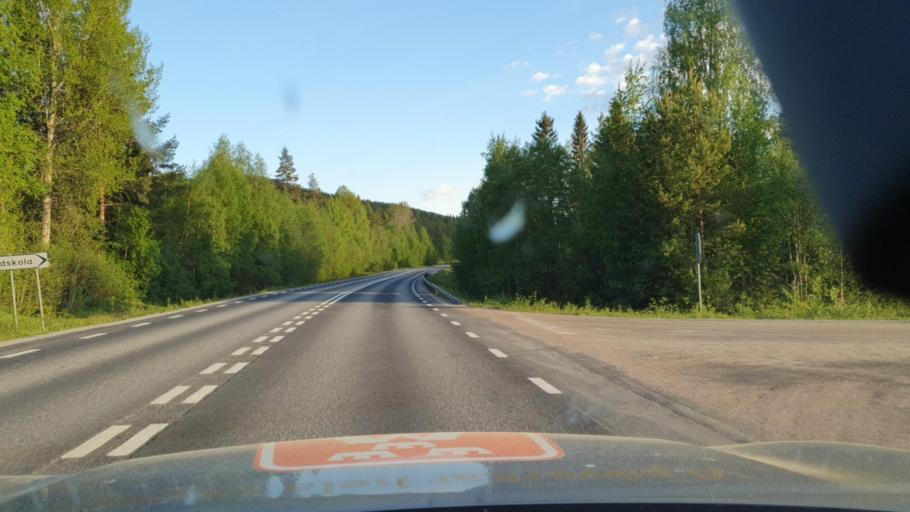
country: SE
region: Vaesternorrland
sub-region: Solleftea Kommun
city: As
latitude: 63.5483
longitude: 16.8449
